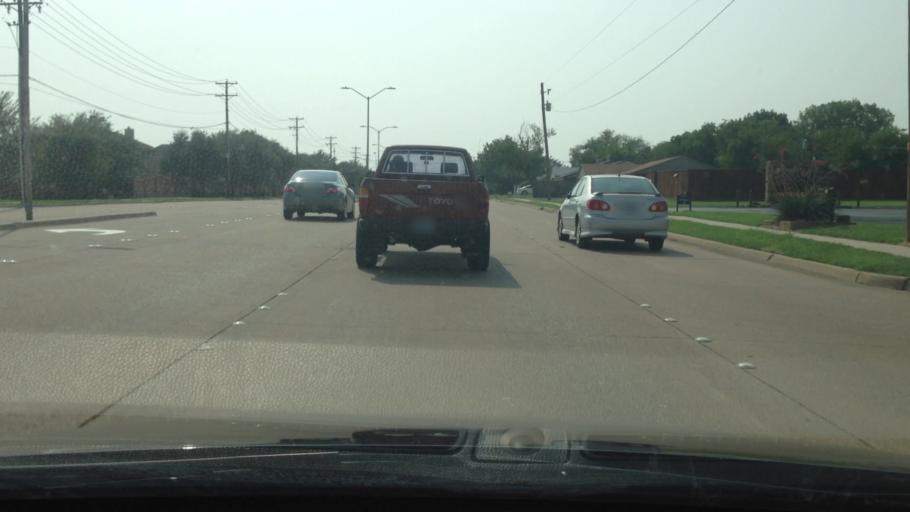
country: US
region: Texas
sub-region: Tarrant County
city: Watauga
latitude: 32.8605
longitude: -97.2324
